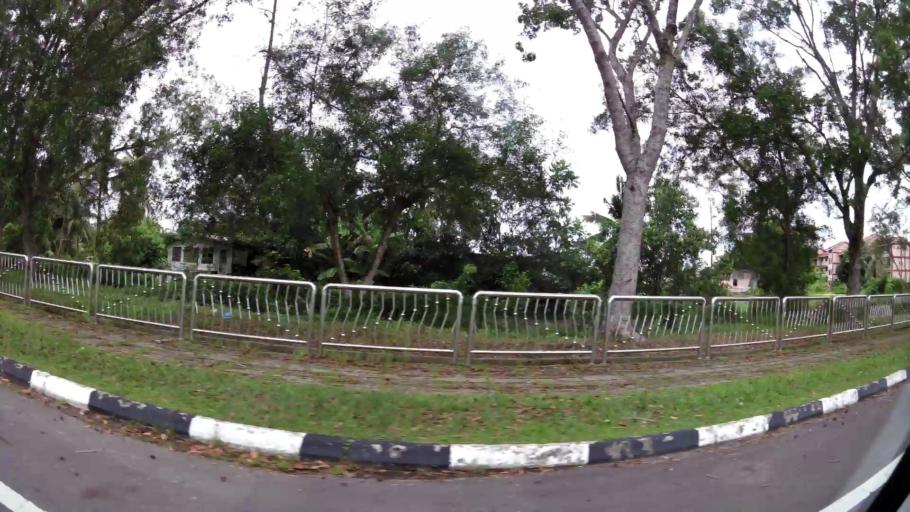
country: BN
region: Brunei and Muara
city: Bandar Seri Begawan
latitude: 4.8982
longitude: 114.9305
